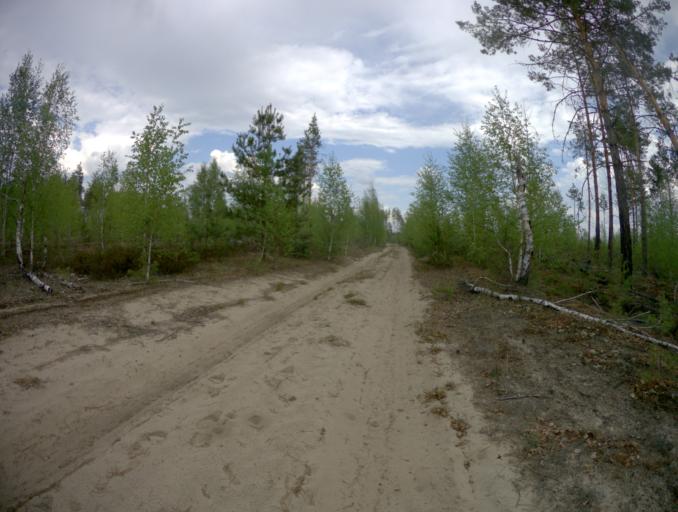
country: RU
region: Ivanovo
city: Talitsy
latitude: 56.4462
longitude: 42.2740
